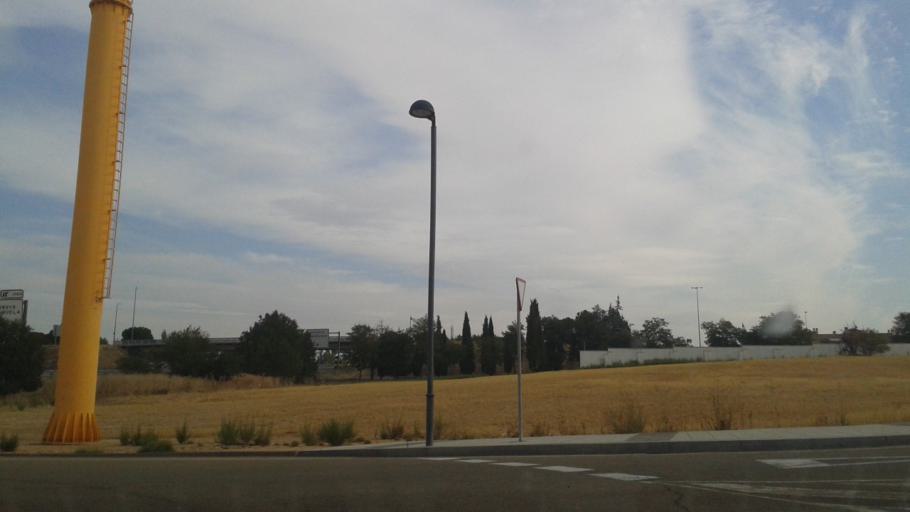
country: ES
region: Castille and Leon
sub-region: Provincia de Valladolid
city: Arroyo
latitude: 41.6111
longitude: -4.7969
